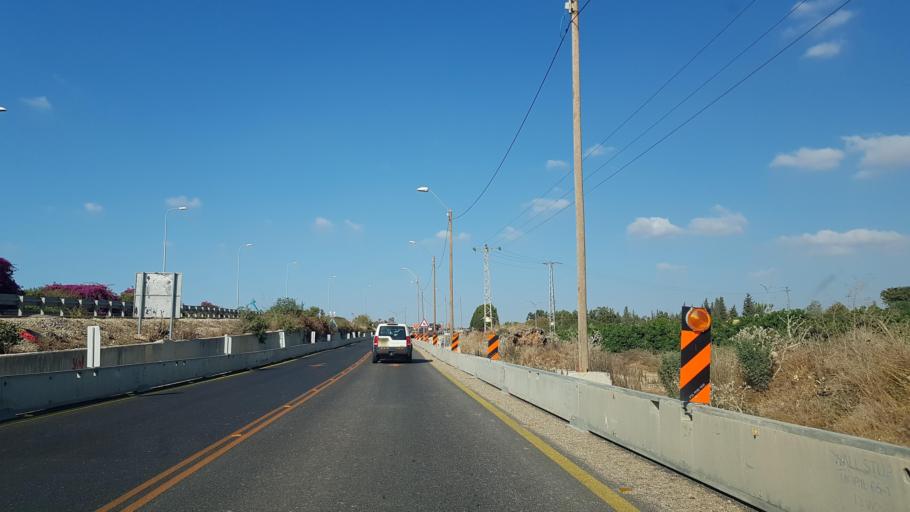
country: PS
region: West Bank
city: Tulkarm
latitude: 32.3345
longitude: 35.0068
